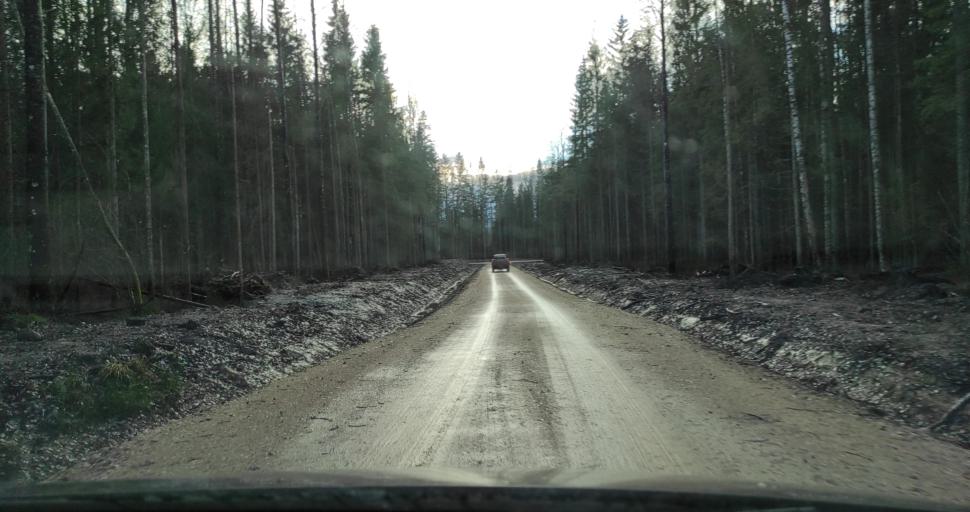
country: LV
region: Skrunda
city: Skrunda
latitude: 56.7423
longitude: 22.1922
